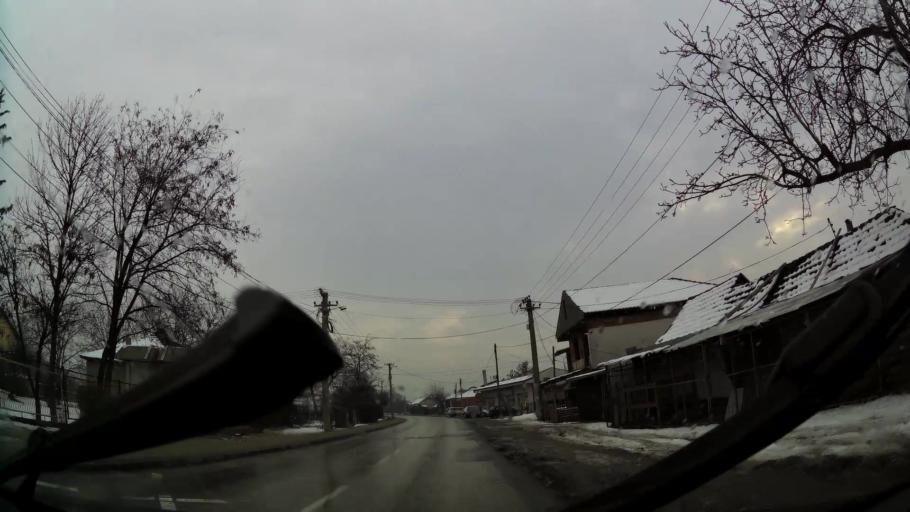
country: MK
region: Saraj
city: Saraj
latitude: 42.0306
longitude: 21.3495
